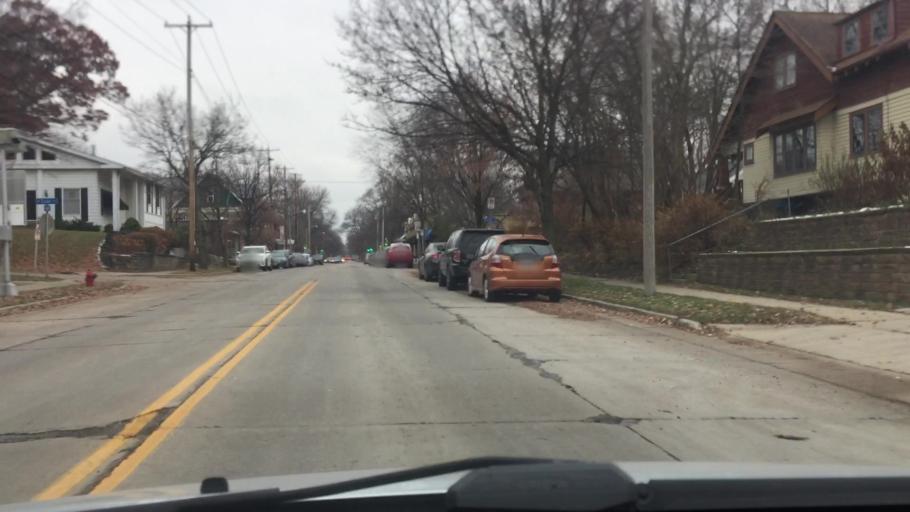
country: US
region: Wisconsin
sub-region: Milwaukee County
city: Wauwatosa
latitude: 43.0411
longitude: -87.9974
